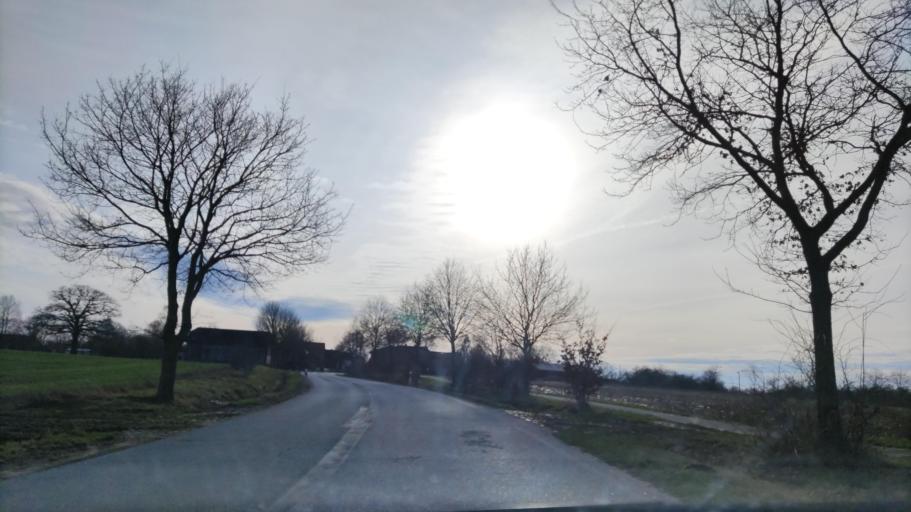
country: DE
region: Schleswig-Holstein
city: Lasbek
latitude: 53.7388
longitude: 10.3636
